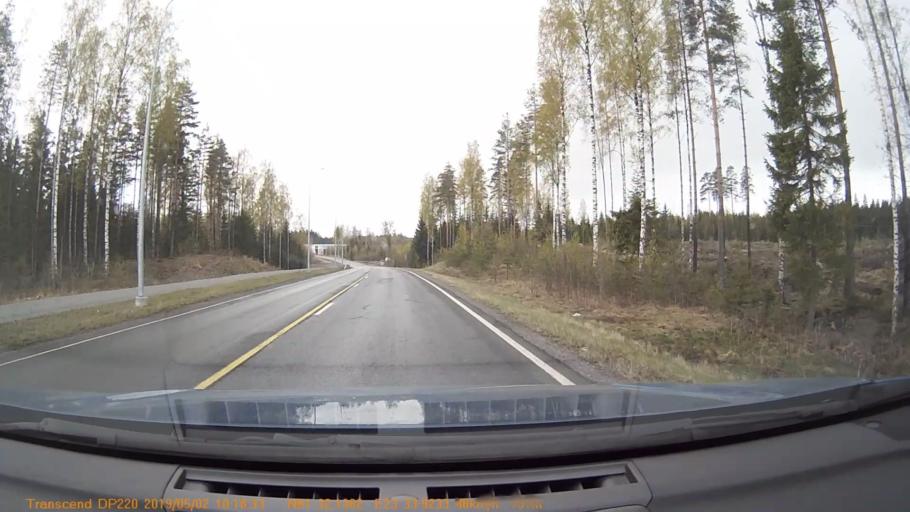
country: FI
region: Pirkanmaa
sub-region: Tampere
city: Yloejaervi
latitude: 61.5357
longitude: 23.5653
